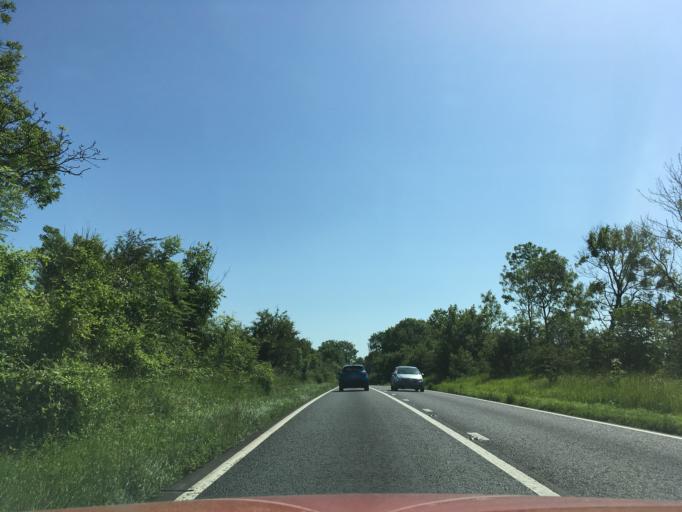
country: GB
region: England
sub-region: Gloucestershire
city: Charlton Kings
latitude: 51.8651
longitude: -2.0063
